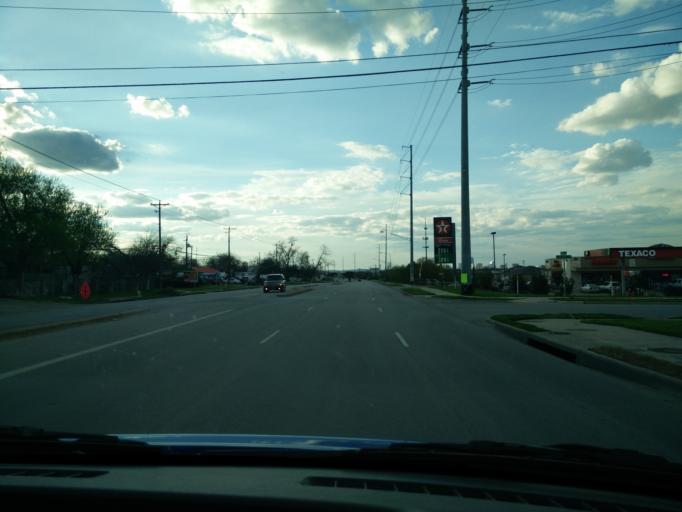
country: US
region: Texas
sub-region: Travis County
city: Austin
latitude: 30.2201
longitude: -97.6931
